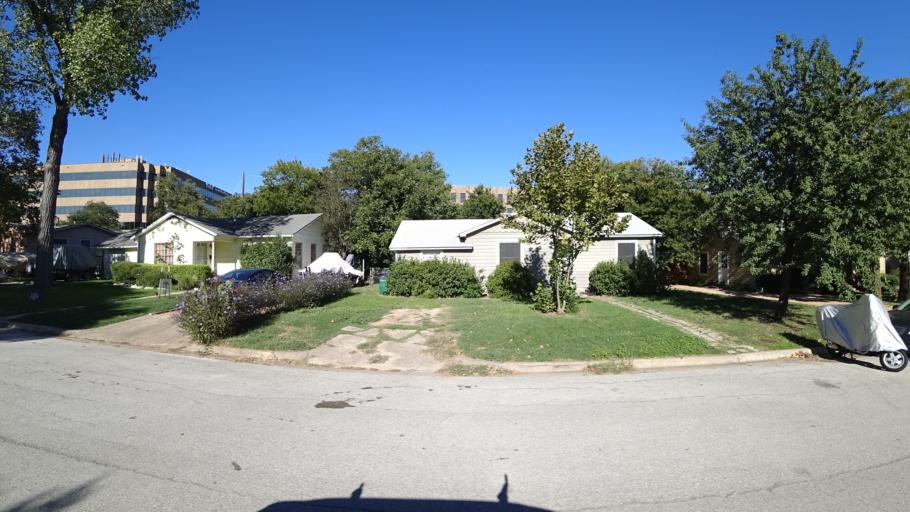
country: US
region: Texas
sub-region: Travis County
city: West Lake Hills
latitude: 30.3337
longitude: -97.7577
